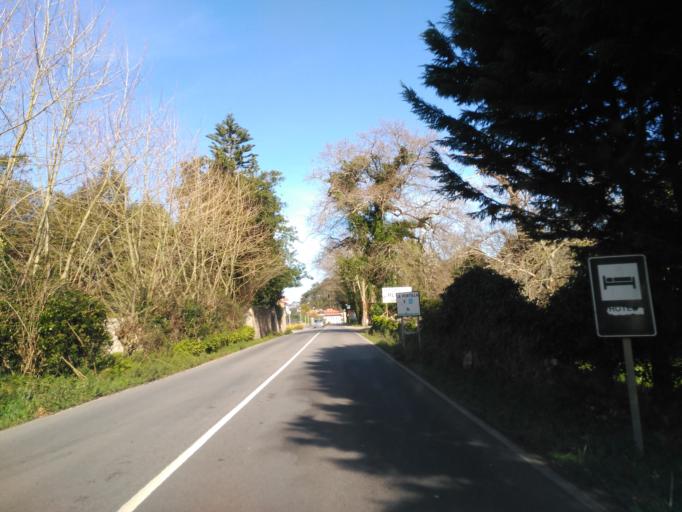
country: ES
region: Asturias
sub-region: Province of Asturias
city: Llanes
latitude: 43.4110
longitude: -4.7553
